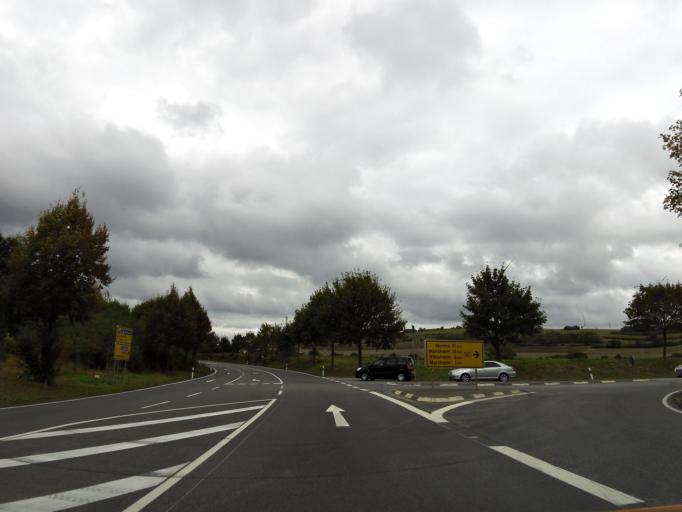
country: DE
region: Rheinland-Pfalz
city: Marnheim
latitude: 49.6372
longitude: 8.0352
